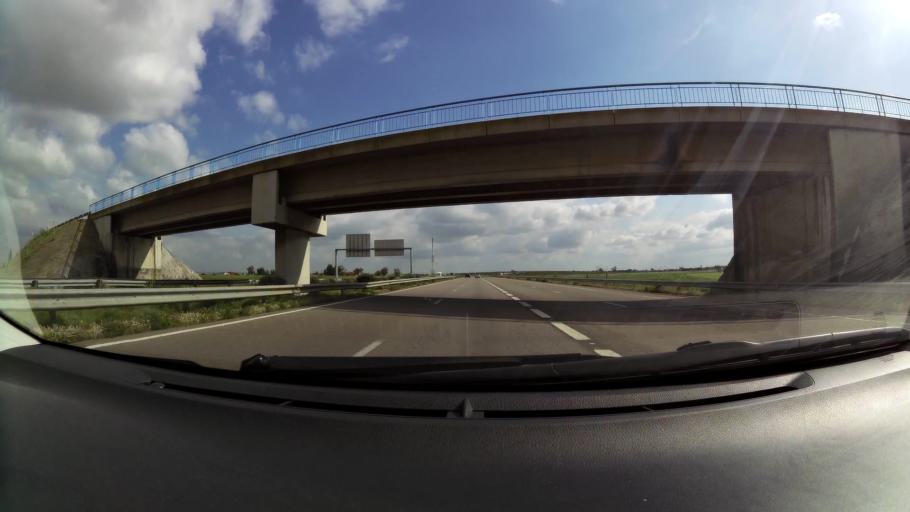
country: MA
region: Chaouia-Ouardigha
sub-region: Settat Province
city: Berrechid
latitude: 33.2796
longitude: -7.5472
